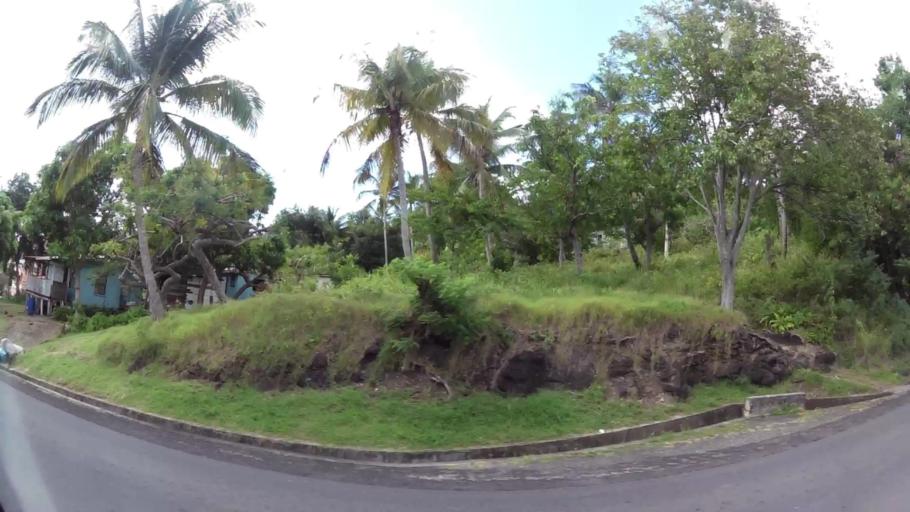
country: LC
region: Laborie Quarter
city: Laborie
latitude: 13.7484
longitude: -60.9869
